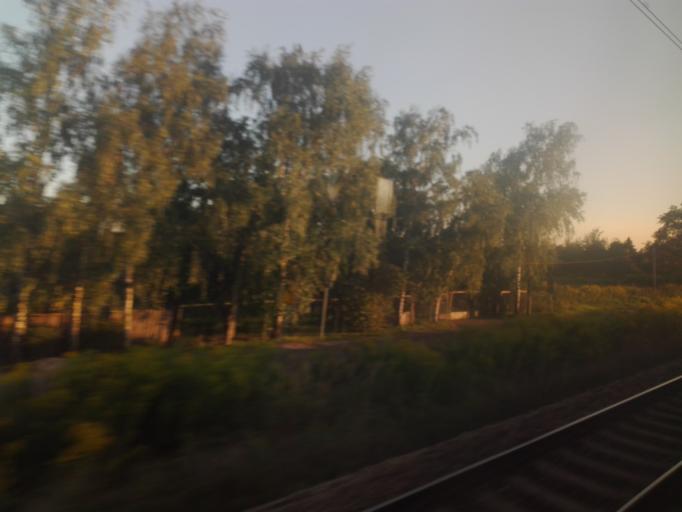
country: PL
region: Masovian Voivodeship
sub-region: Powiat warszawski zachodni
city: Jozefow
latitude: 52.2039
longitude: 20.7253
